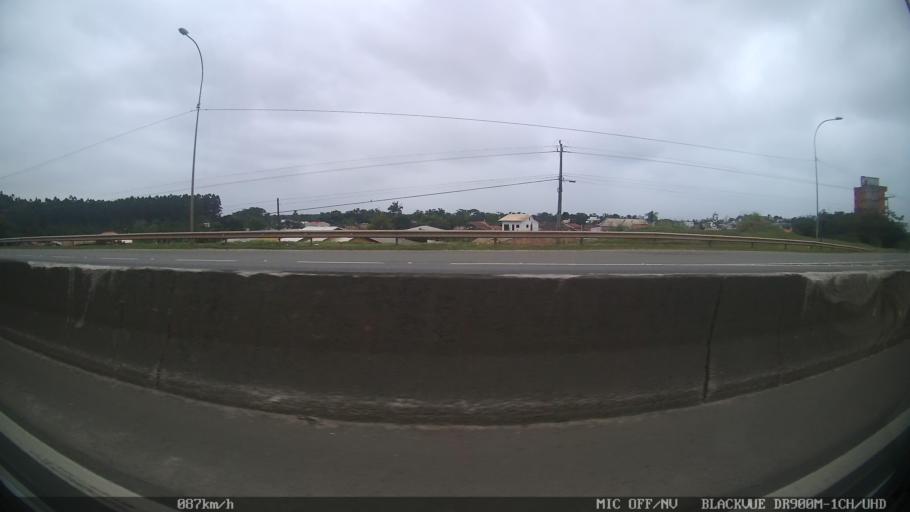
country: BR
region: Santa Catarina
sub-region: Barra Velha
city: Barra Velha
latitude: -26.6357
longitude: -48.6984
